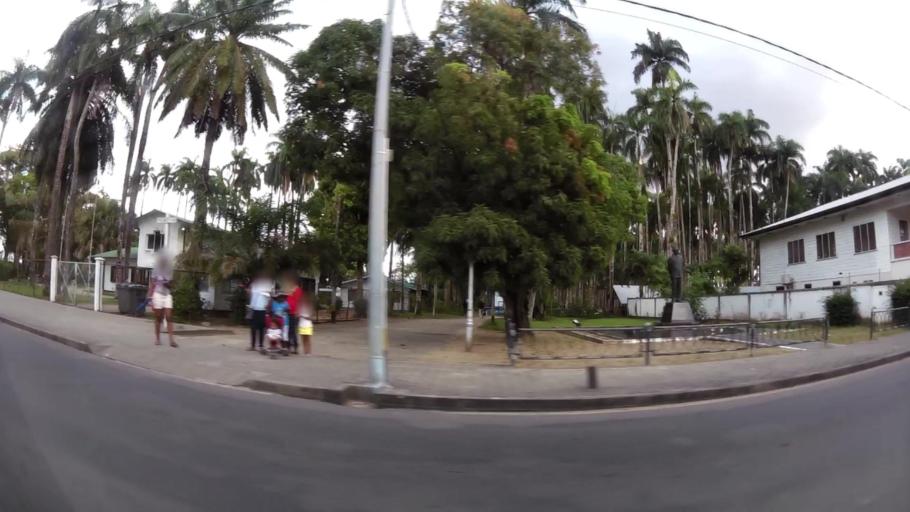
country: SR
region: Paramaribo
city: Paramaribo
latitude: 5.8267
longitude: -55.1496
